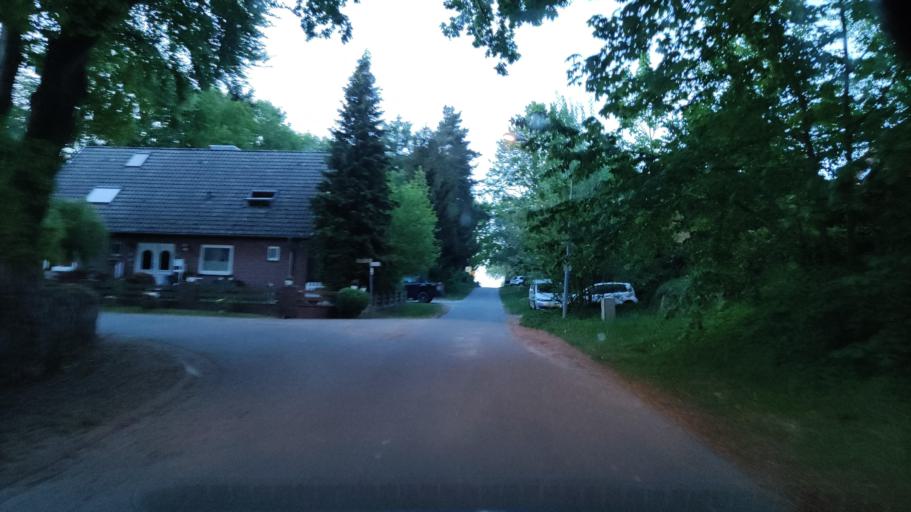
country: DE
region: Lower Saxony
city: Egestorf
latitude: 53.1983
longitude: 10.1004
